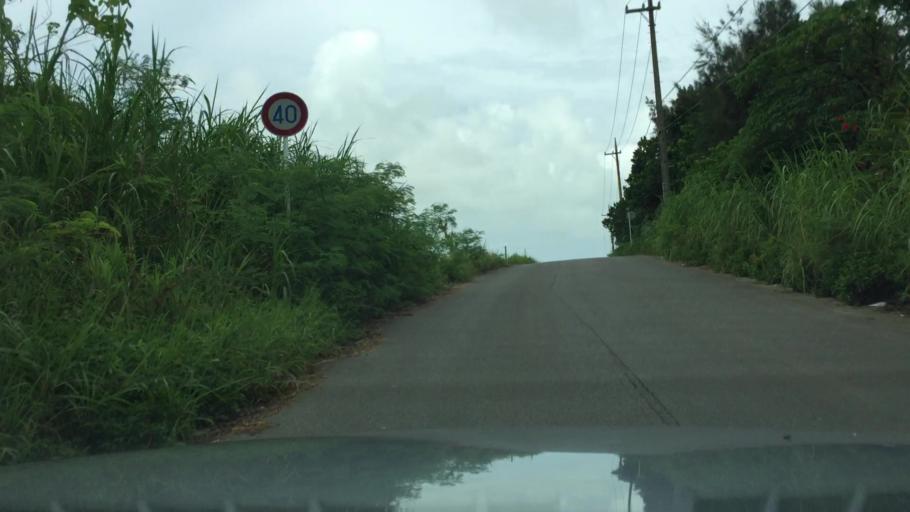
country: JP
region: Okinawa
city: Ishigaki
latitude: 24.4012
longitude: 124.2108
